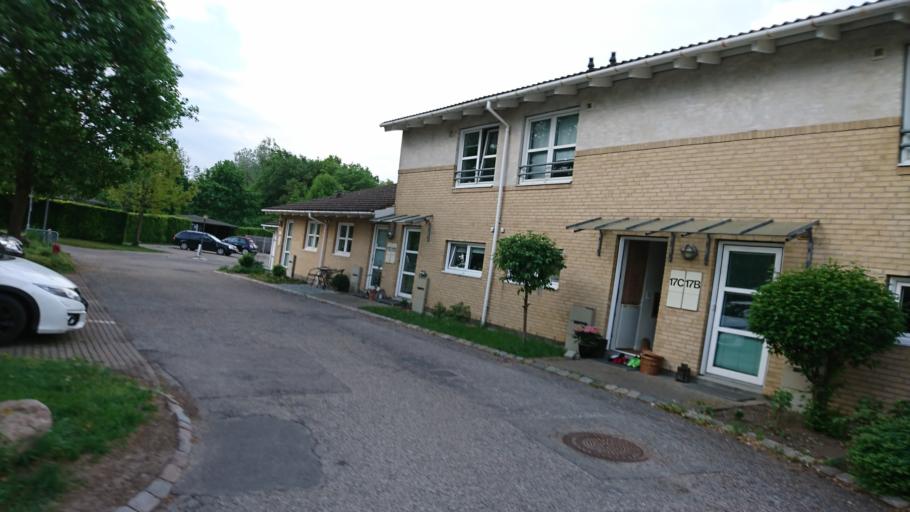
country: DK
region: Capital Region
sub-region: Ballerup Kommune
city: Ballerup
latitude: 55.7532
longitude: 12.4034
